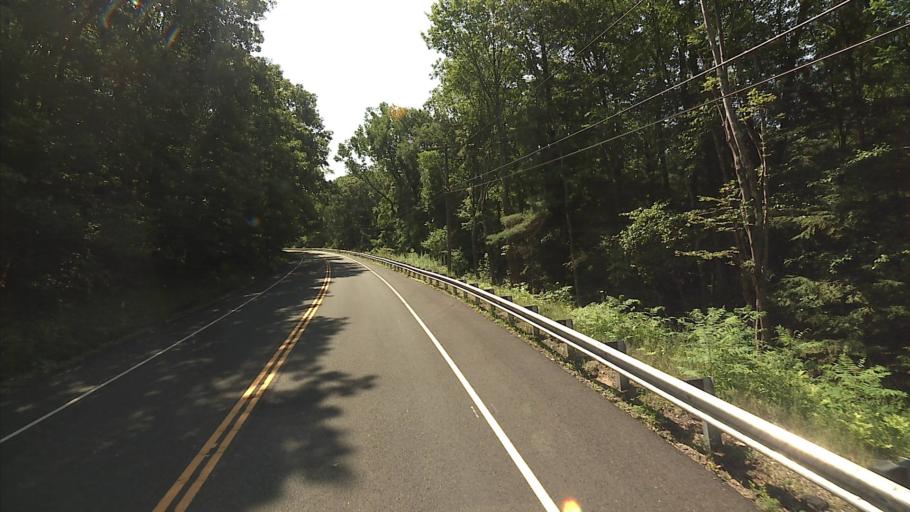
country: US
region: Massachusetts
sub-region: Berkshire County
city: New Marlborough
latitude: 42.0379
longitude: -73.2126
